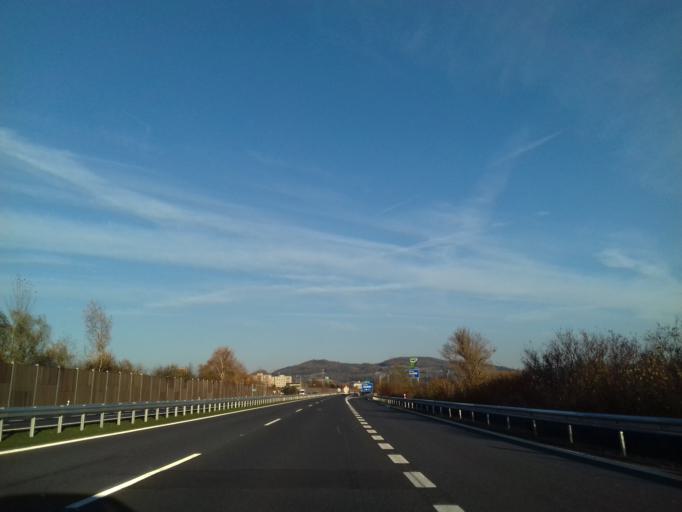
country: CZ
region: Central Bohemia
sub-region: Okres Beroun
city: Beroun
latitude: 49.9551
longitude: 14.0580
